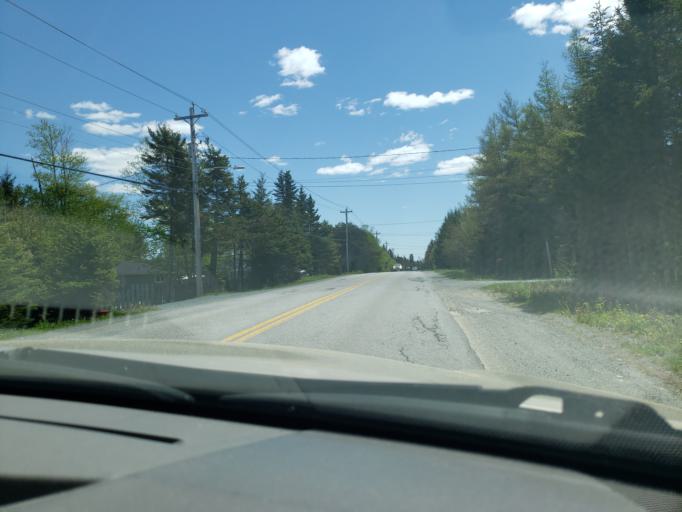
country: CA
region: Nova Scotia
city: Cole Harbour
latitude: 44.7332
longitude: -63.3087
